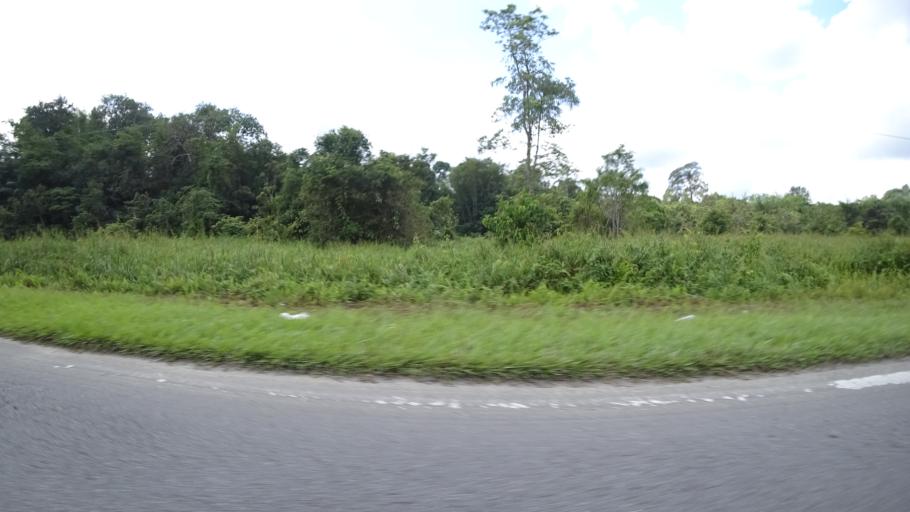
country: BN
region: Tutong
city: Tutong
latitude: 4.6987
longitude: 114.8028
